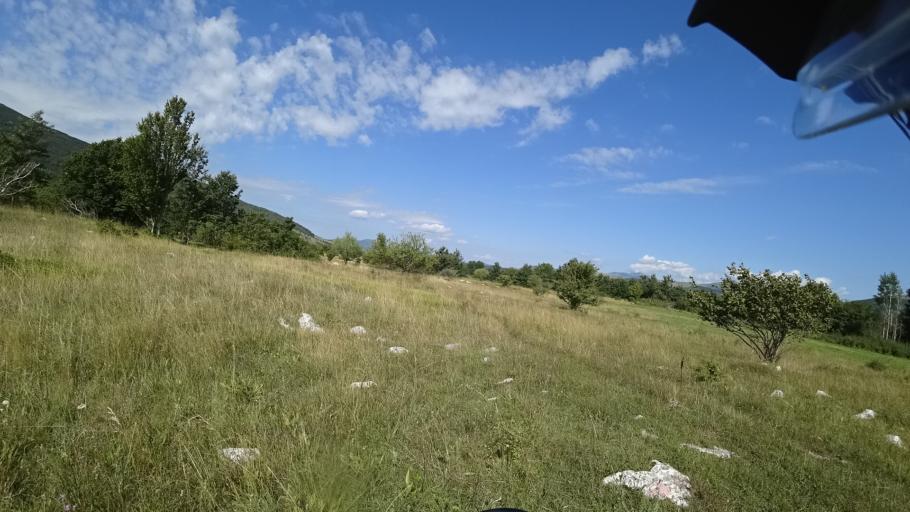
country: HR
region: Zadarska
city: Gracac
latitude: 44.3360
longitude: 15.9588
